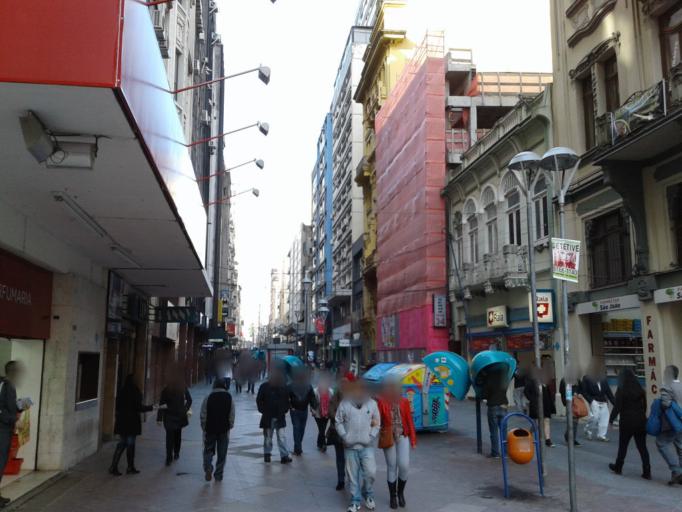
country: BR
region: Rio Grande do Sul
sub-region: Porto Alegre
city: Porto Alegre
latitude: -30.0301
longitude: -51.2301
